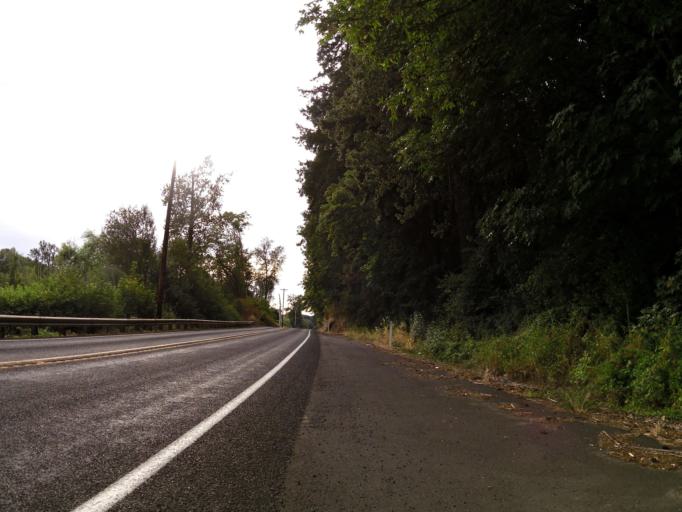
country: US
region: Washington
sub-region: Cowlitz County
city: West Longview
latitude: 46.1885
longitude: -123.0935
